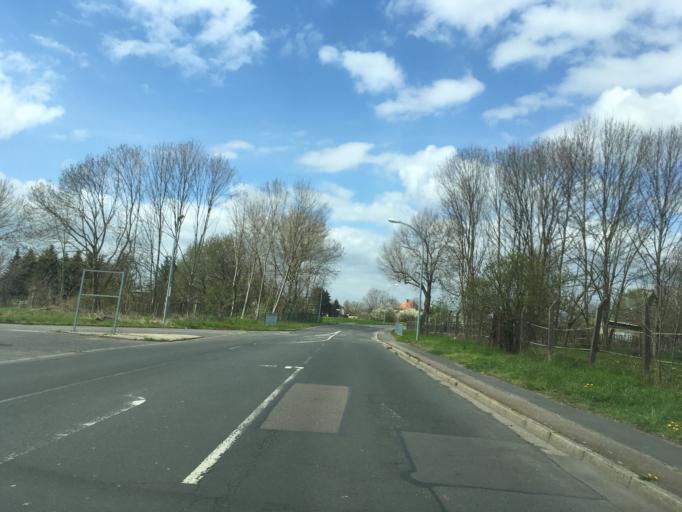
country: DE
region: Saxony
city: Delitzsch
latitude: 51.5178
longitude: 12.3224
